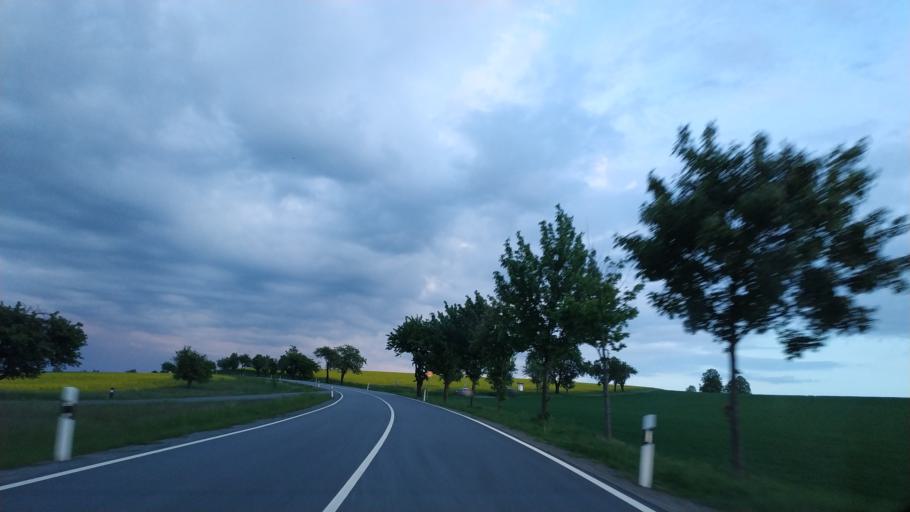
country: DE
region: Saxony
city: Hohnstein
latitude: 50.9962
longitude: 14.0761
